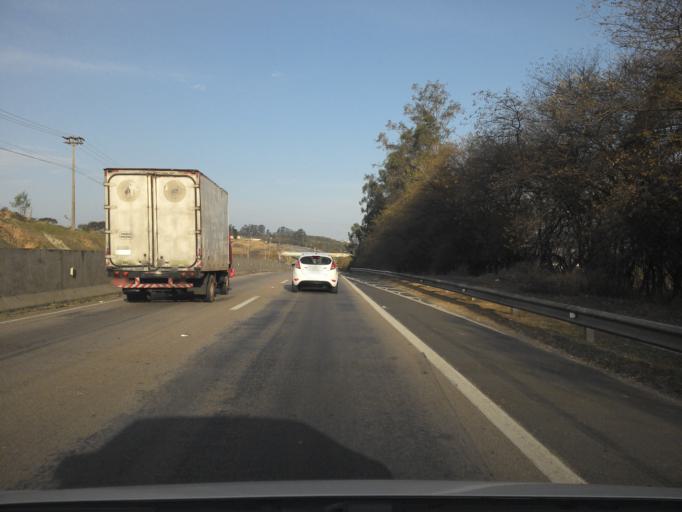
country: BR
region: Sao Paulo
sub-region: Campinas
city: Campinas
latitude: -22.8896
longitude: -47.1415
